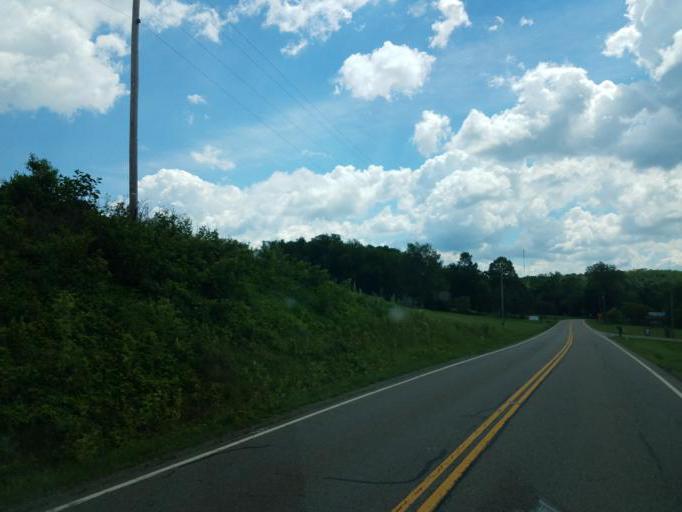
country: US
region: Ohio
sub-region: Knox County
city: Oak Hill
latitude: 40.4023
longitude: -82.2846
